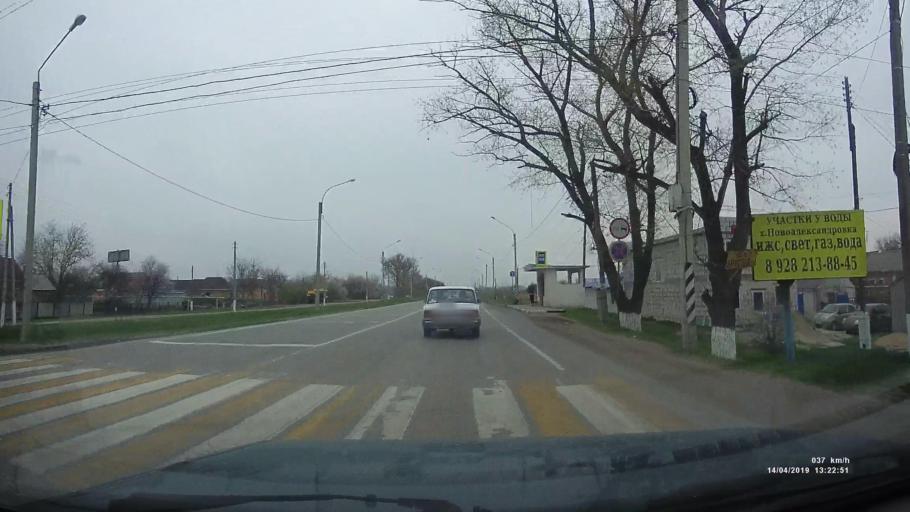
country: RU
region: Rostov
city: Kuleshovka
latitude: 47.0830
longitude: 39.5073
